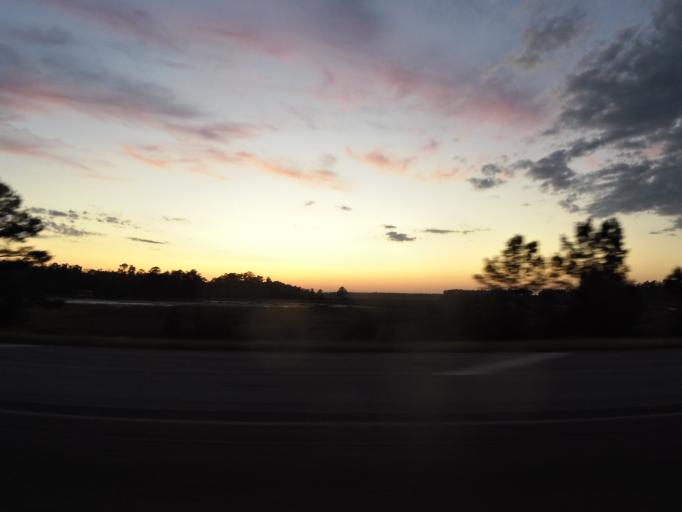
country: US
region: Georgia
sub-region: Liberty County
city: Midway
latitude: 31.8059
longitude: -81.3680
